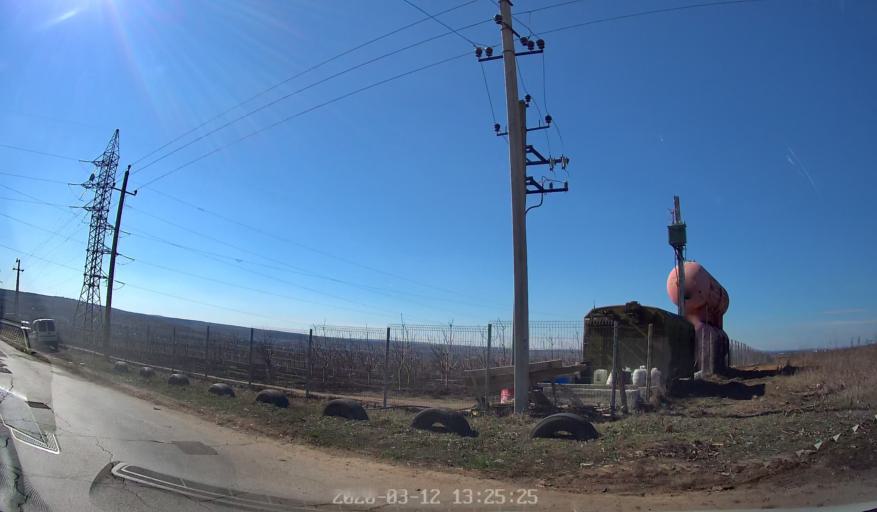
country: MD
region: Laloveni
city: Ialoveni
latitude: 46.9427
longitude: 28.8194
